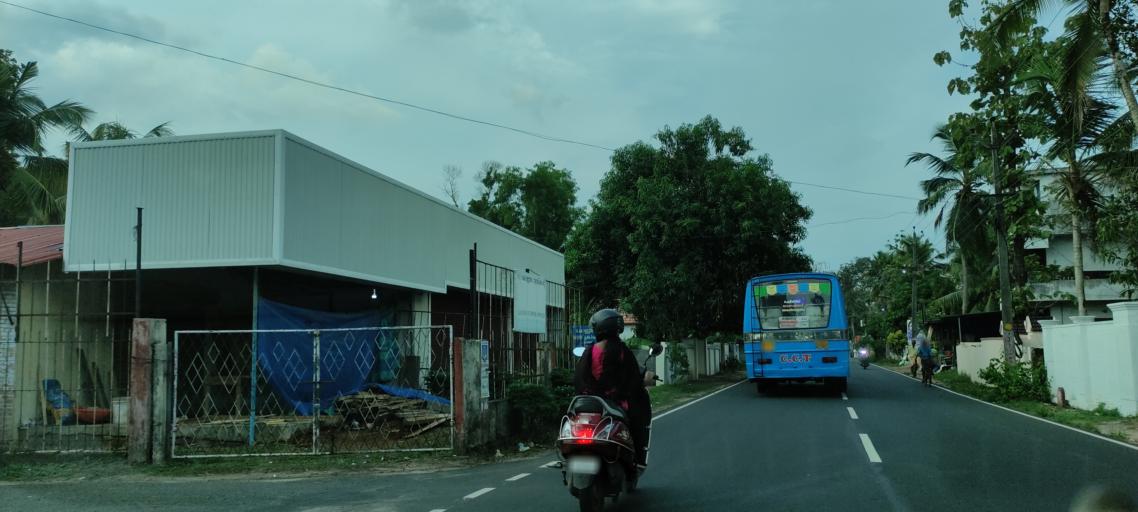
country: IN
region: Kerala
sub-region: Alappuzha
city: Kutiatodu
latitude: 9.7870
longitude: 76.3594
